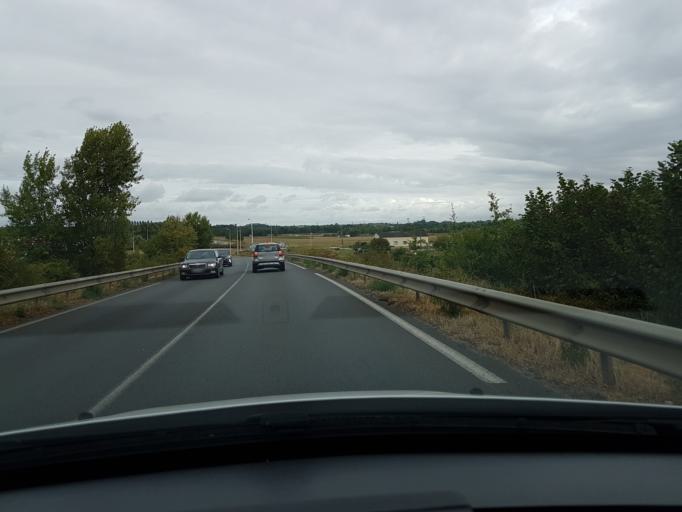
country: FR
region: Centre
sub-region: Departement d'Indre-et-Loire
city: La Ville-aux-Dames
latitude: 47.3913
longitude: 0.7880
